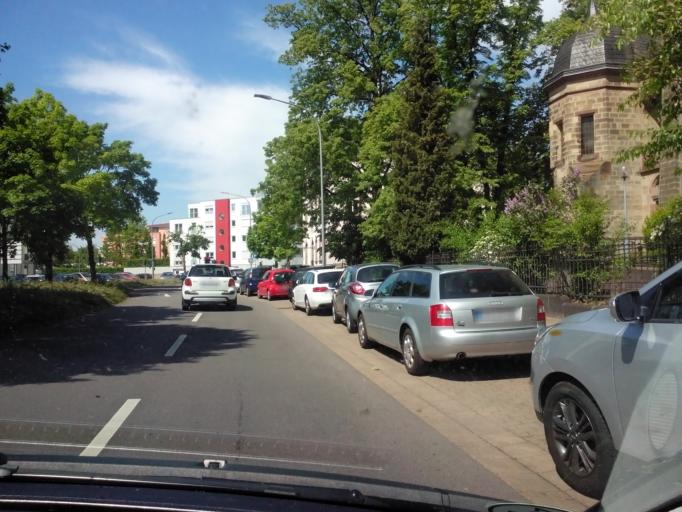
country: DE
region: Saarland
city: Saarlouis
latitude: 49.3129
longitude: 6.7483
